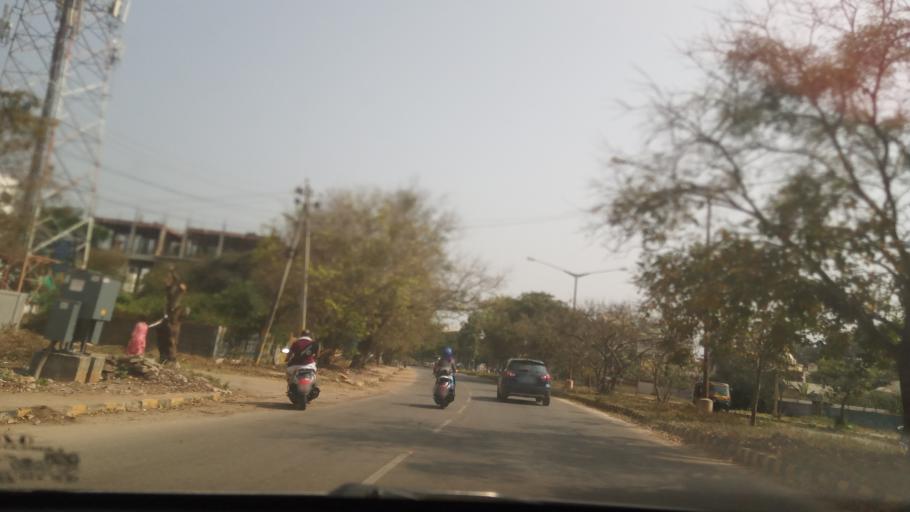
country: IN
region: Karnataka
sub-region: Mysore
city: Mysore
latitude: 12.2903
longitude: 76.6226
